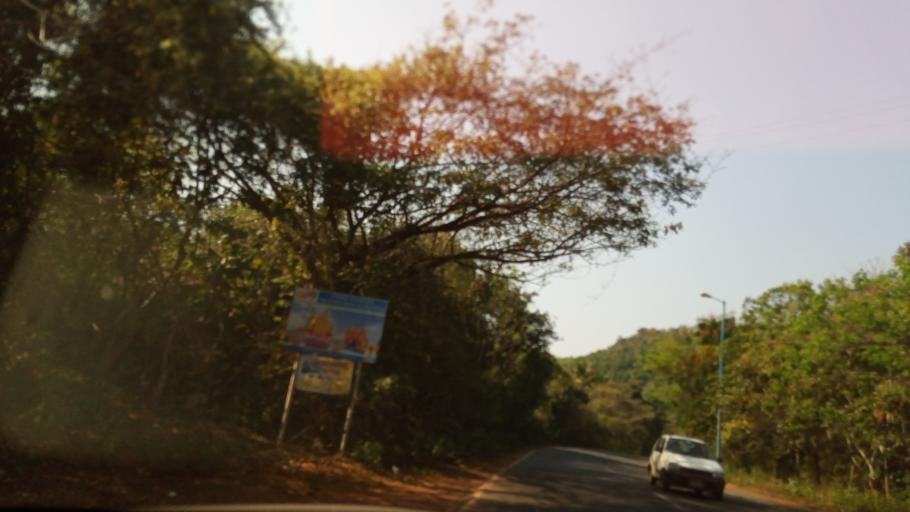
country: IN
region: Goa
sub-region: North Goa
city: Bandora
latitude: 15.4451
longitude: 73.9740
